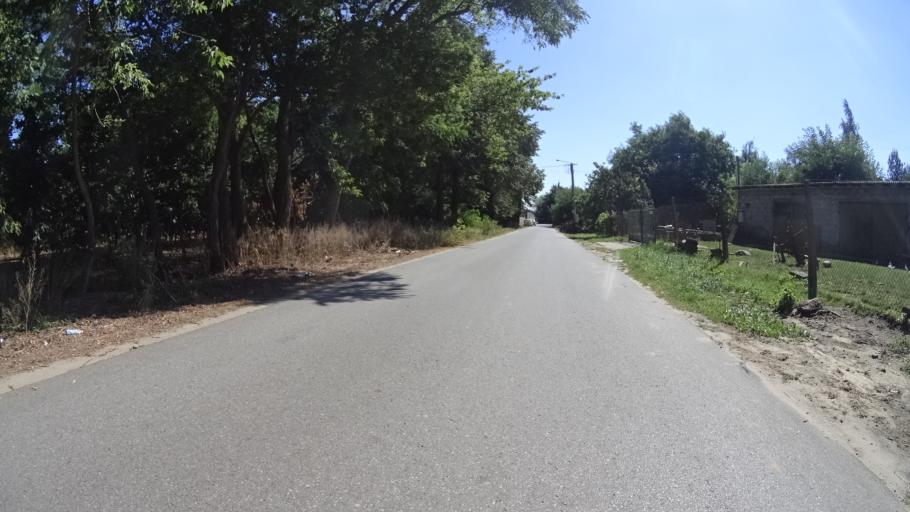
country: PL
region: Masovian Voivodeship
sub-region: Powiat bialobrzeski
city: Bialobrzegi
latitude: 51.6704
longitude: 20.9142
